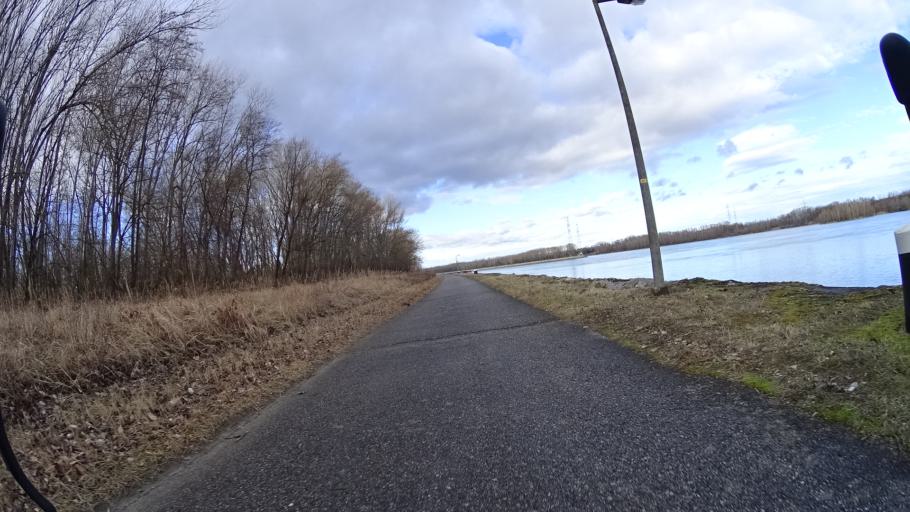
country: AT
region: Lower Austria
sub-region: Politischer Bezirk Tulln
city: Kirchberg am Wagram
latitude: 48.3672
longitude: 15.8744
